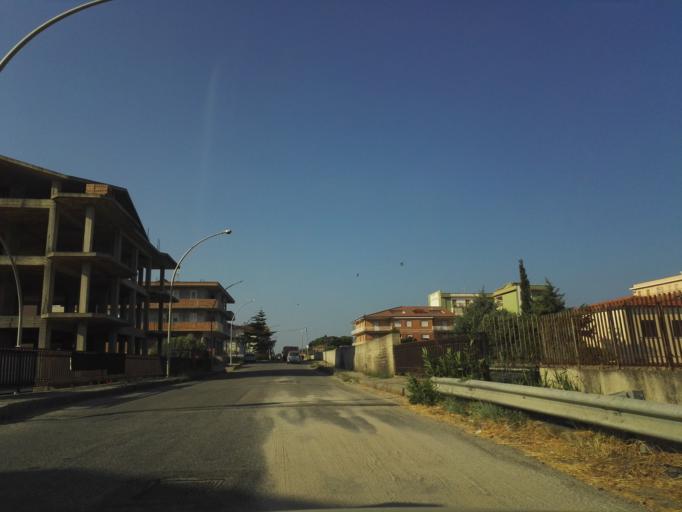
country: IT
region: Calabria
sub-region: Provincia di Reggio Calabria
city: Monasterace Marina
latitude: 38.4326
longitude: 16.5721
